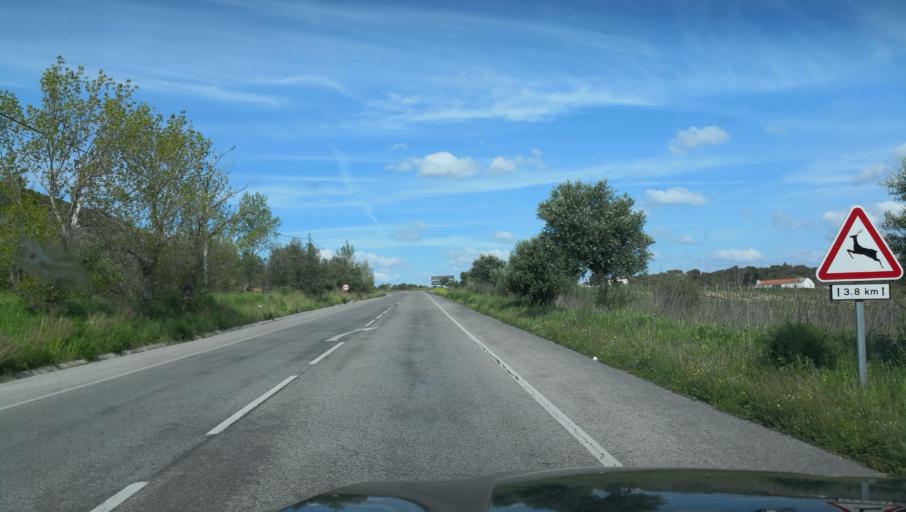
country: PT
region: Setubal
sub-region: Palmela
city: Quinta do Anjo
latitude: 38.5232
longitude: -8.9546
